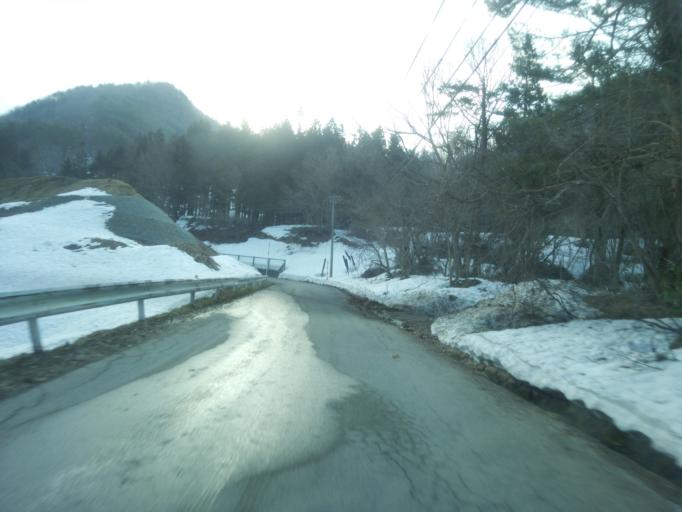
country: JP
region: Fukushima
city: Kitakata
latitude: 37.7265
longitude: 139.9390
